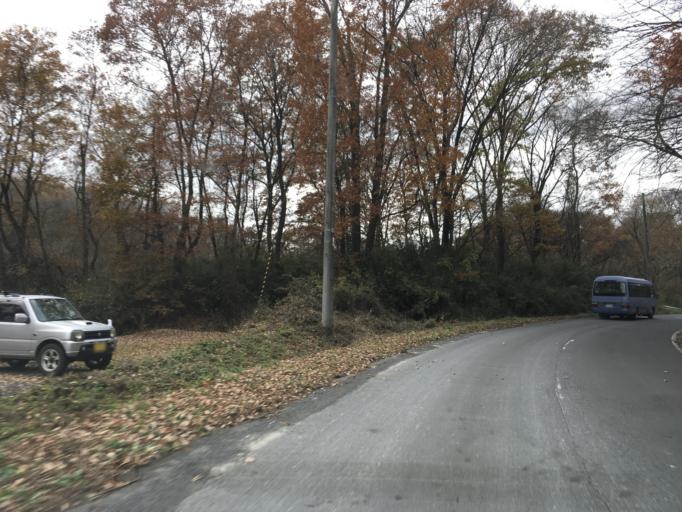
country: JP
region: Iwate
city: Ichinoseki
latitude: 38.8417
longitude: 141.0511
